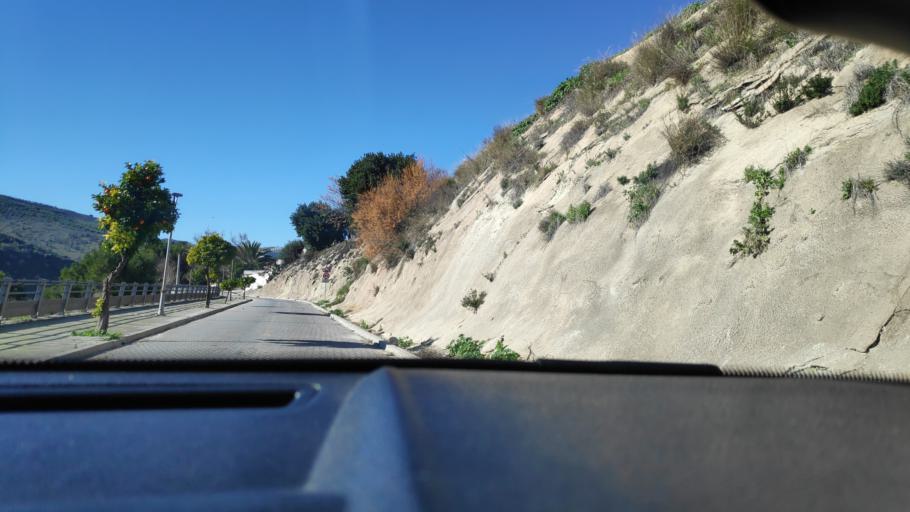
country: ES
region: Andalusia
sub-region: Province of Cordoba
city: Baena
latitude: 37.6117
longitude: -4.3279
